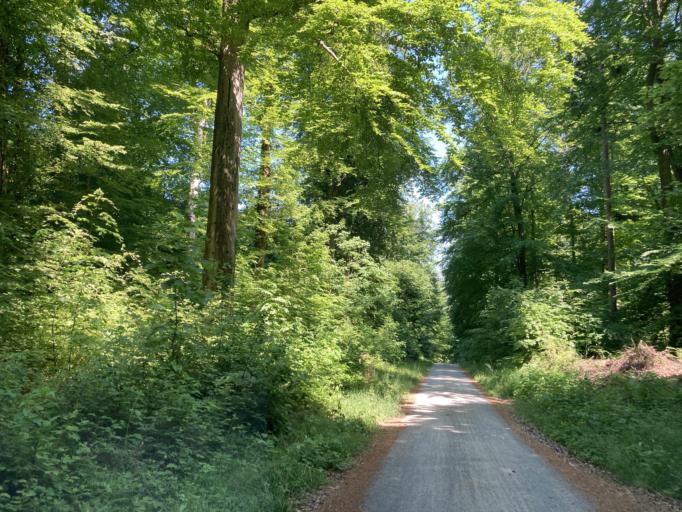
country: DE
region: Baden-Wuerttemberg
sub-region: Karlsruhe Region
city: Joehlingen
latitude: 49.0100
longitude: 8.5778
